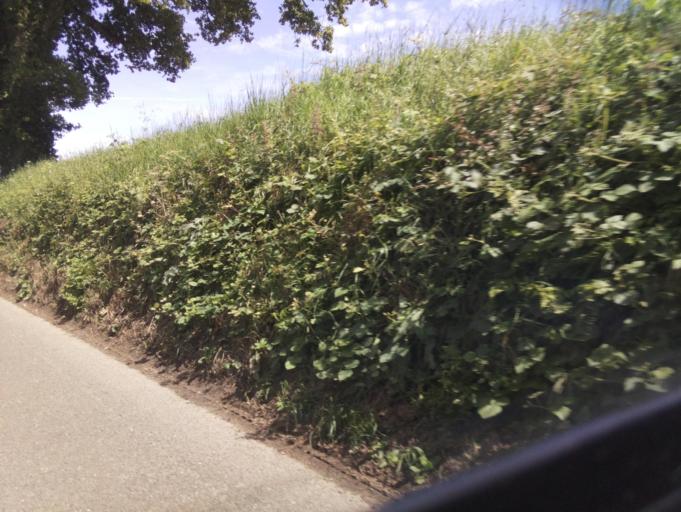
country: GB
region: England
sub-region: Devon
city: Uffculme
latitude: 50.8486
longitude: -3.3238
